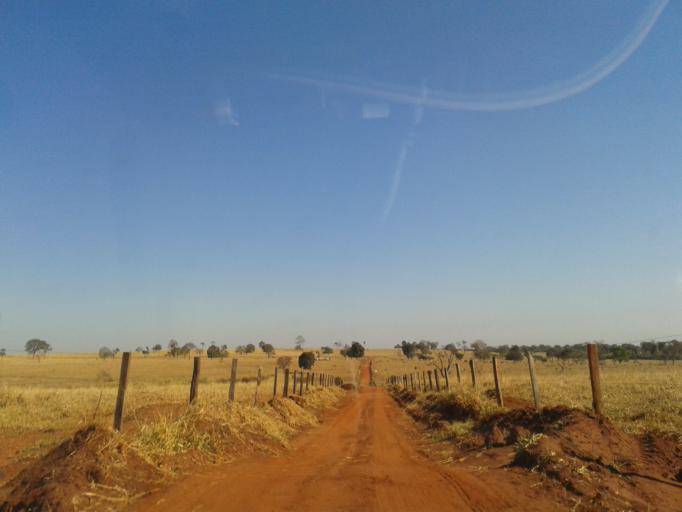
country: BR
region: Minas Gerais
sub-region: Santa Vitoria
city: Santa Vitoria
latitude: -19.0538
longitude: -49.9321
